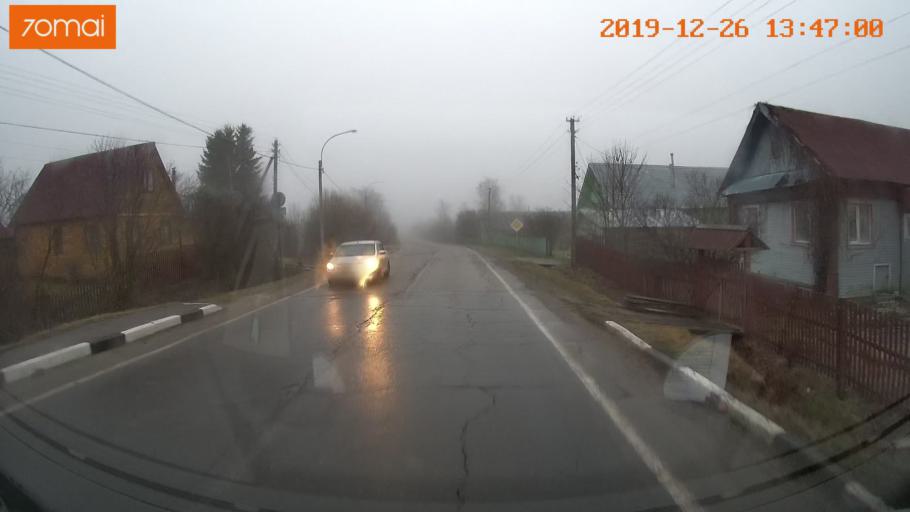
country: RU
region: Vologda
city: Sheksna
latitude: 58.6878
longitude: 38.5304
